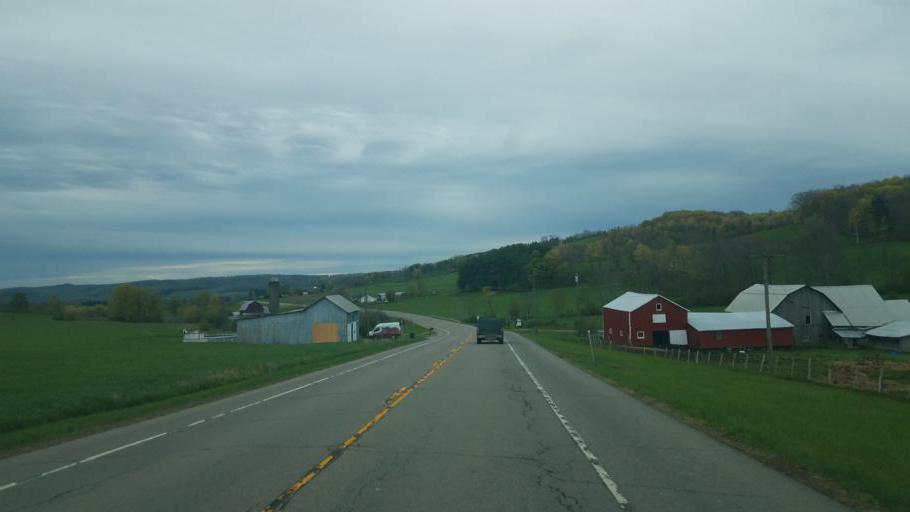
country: US
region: New York
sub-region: Steuben County
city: Canisteo
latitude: 42.1559
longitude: -77.5195
